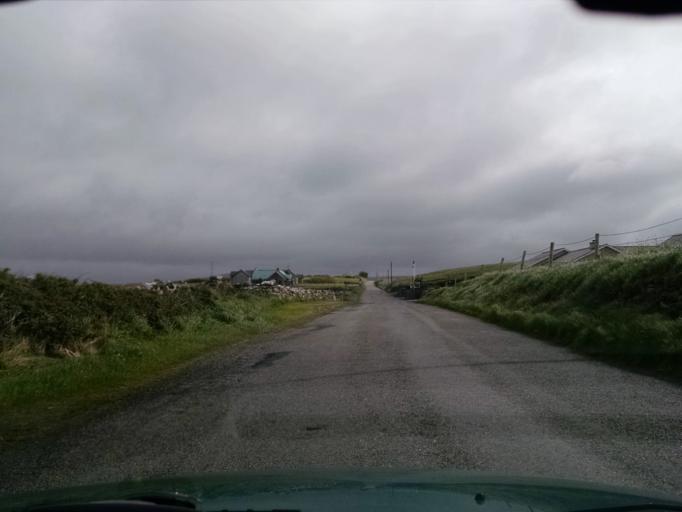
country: IE
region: Connaught
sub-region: County Galway
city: Bearna
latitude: 53.0335
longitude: -9.3631
